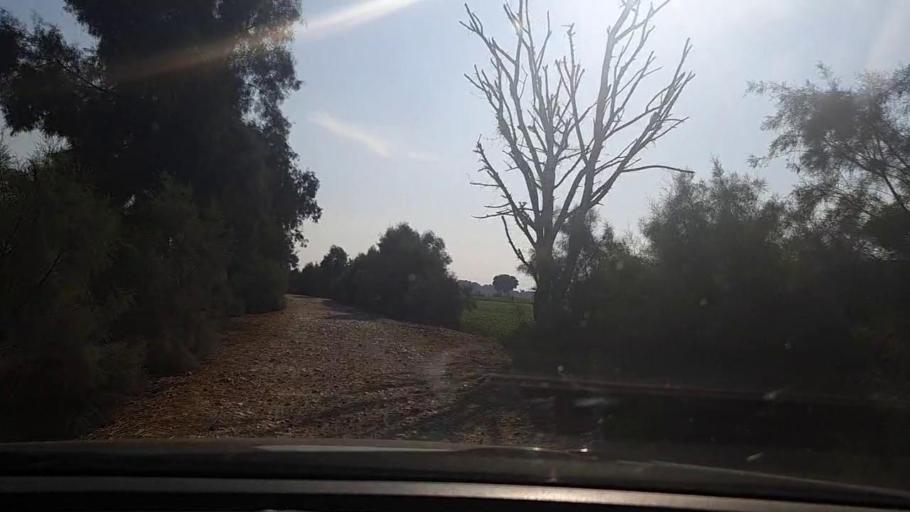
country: PK
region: Sindh
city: Sehwan
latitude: 26.3107
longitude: 68.0014
